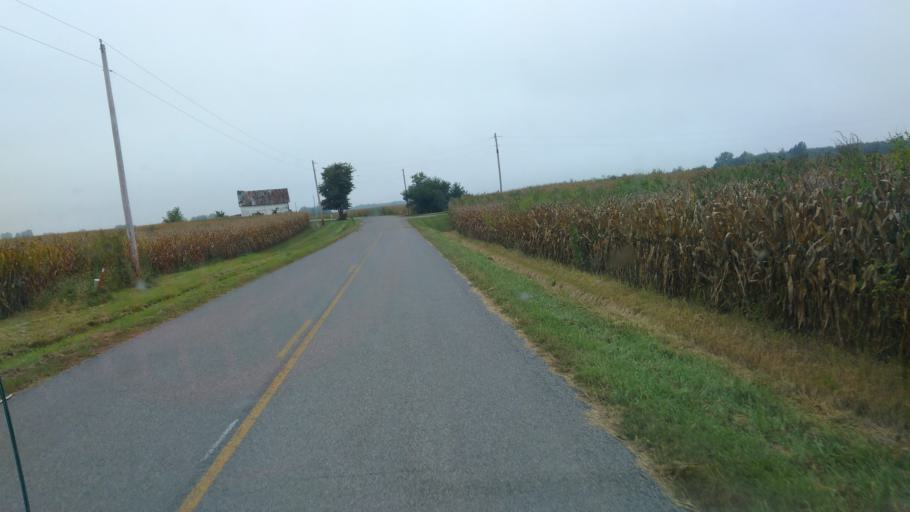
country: US
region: Ohio
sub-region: Logan County
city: Northwood
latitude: 40.4794
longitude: -83.5799
